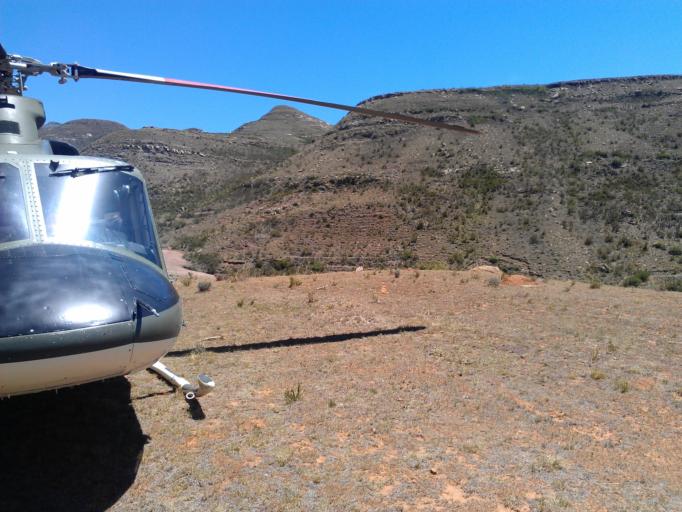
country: LS
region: Qacha's Nek
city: Qacha's Nek
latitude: -30.0396
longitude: 28.6055
